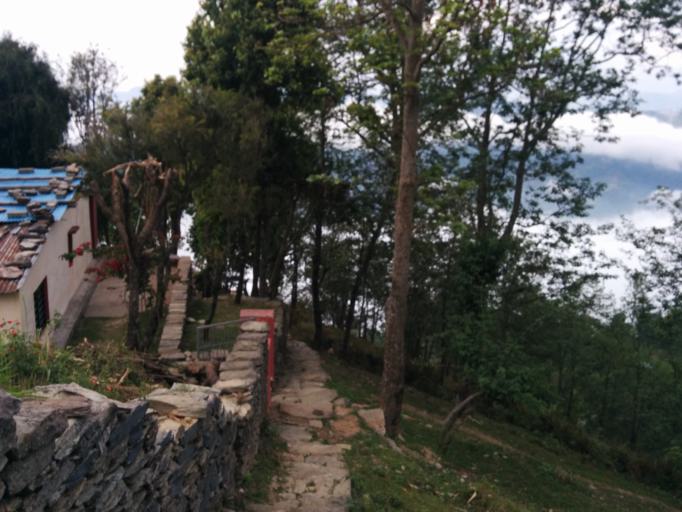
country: NP
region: Western Region
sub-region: Gandaki Zone
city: Pokhara
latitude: 28.2382
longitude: 83.9500
